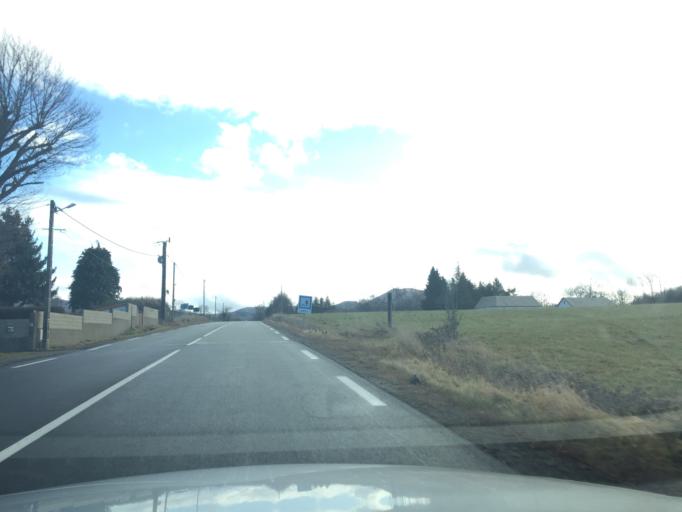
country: FR
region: Auvergne
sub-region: Departement du Puy-de-Dome
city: Saint-Ours
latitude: 45.8337
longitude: 2.8853
